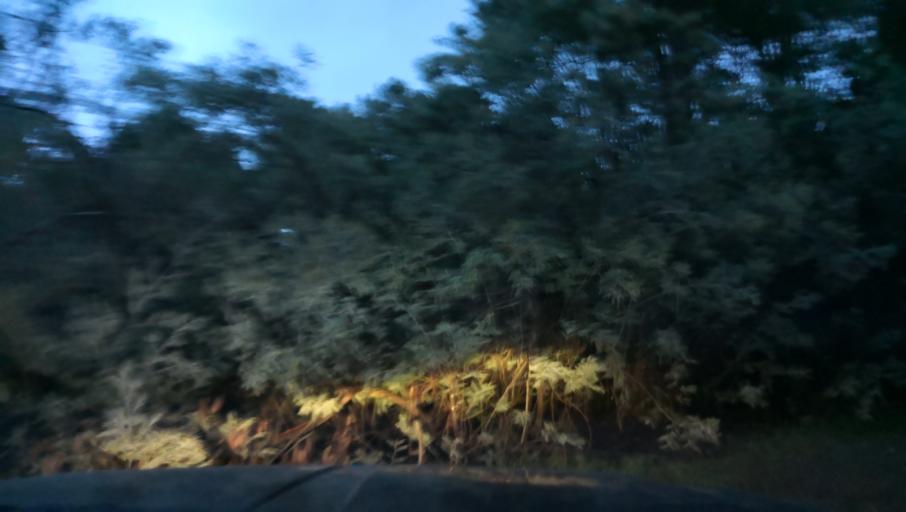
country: PT
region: Vila Real
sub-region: Vila Real
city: Vila Real
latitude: 41.2723
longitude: -7.7341
